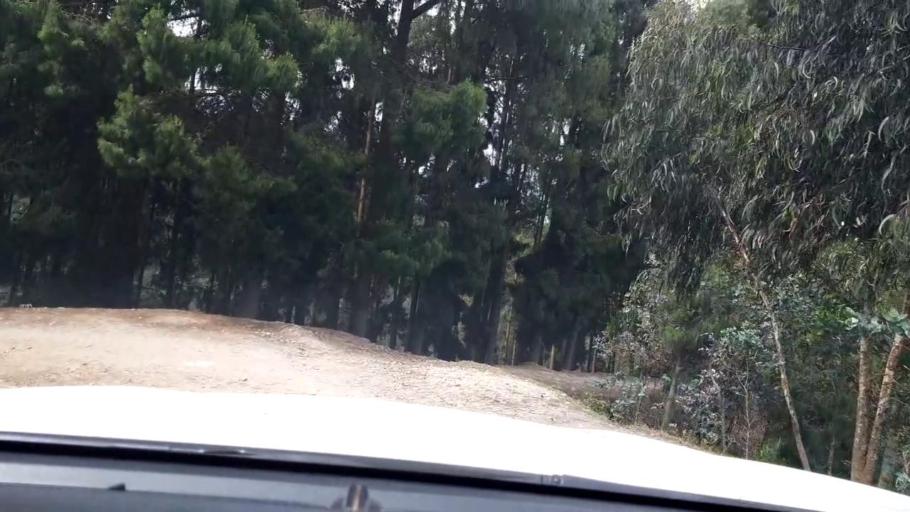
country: RW
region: Western Province
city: Kibuye
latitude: -1.8759
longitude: 29.4541
